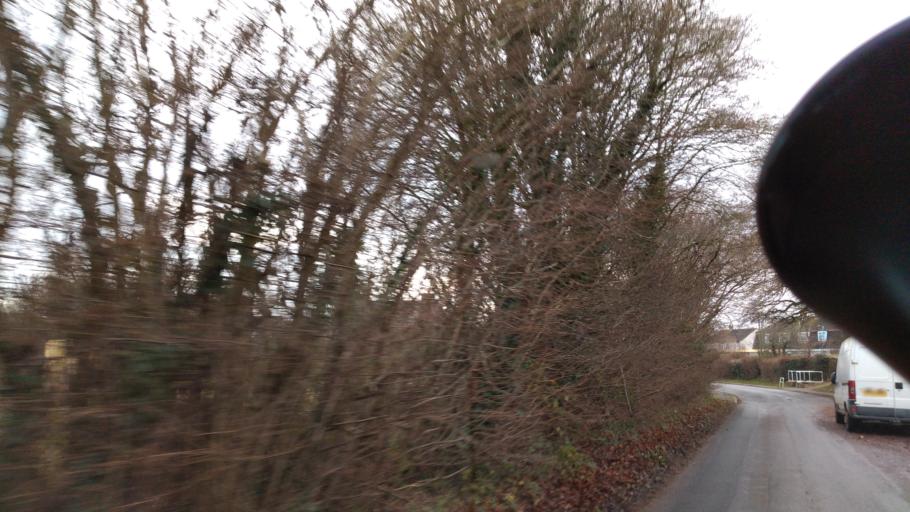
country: GB
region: England
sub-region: Borough of Swindon
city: Highworth
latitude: 51.5922
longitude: -1.7249
